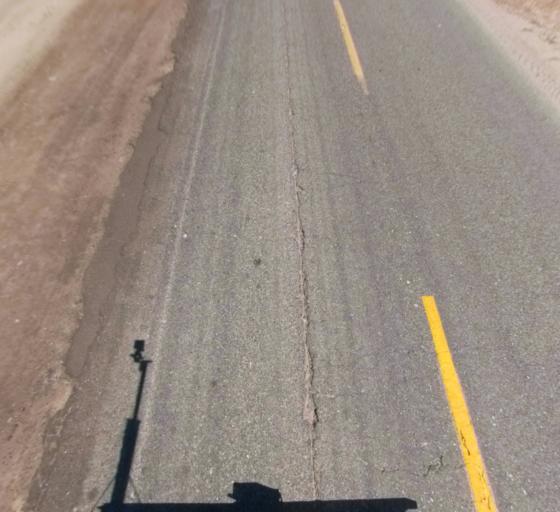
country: US
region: California
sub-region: Fresno County
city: Biola
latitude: 36.8605
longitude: -120.0013
